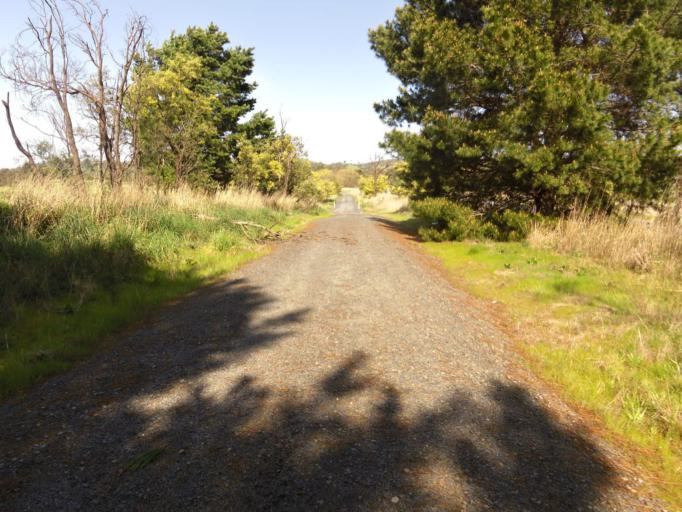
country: AU
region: Victoria
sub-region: Murrindindi
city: Alexandra
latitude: -37.0100
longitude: 145.7543
